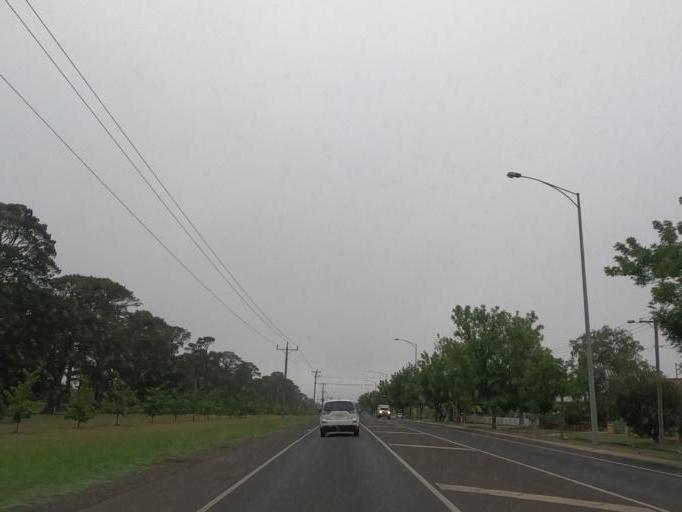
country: AU
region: Victoria
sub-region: Ballarat North
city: Newington
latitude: -37.5596
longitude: 143.8180
